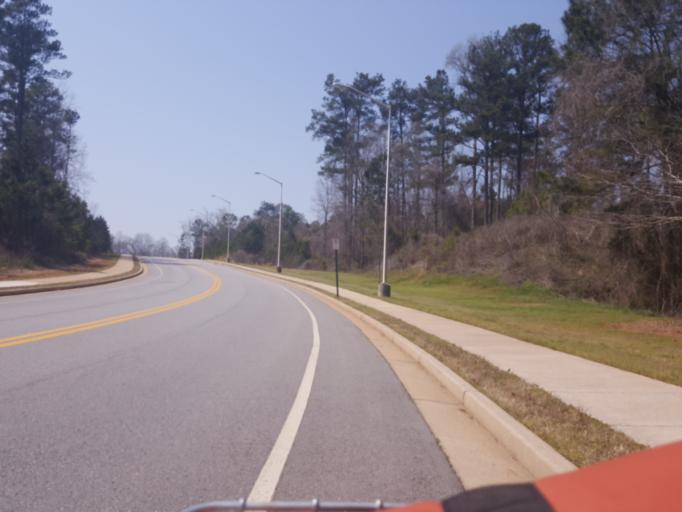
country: US
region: Georgia
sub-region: Carroll County
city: Carrollton
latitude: 33.5757
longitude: -85.1062
